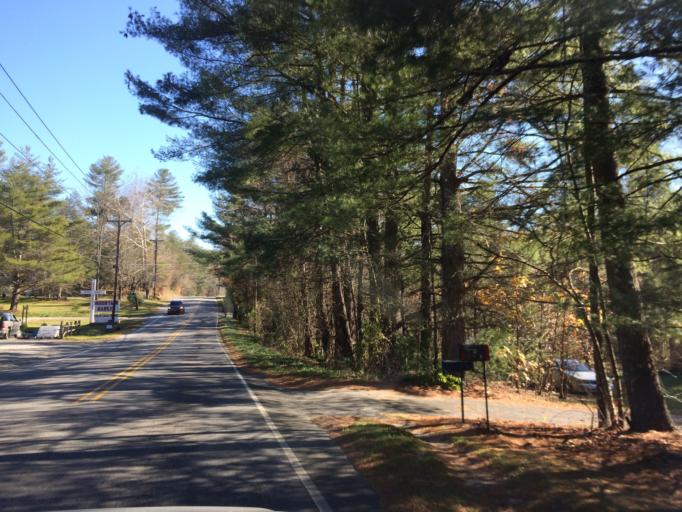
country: US
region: North Carolina
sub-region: Henderson County
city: Laurel Park
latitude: 35.3282
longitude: -82.5087
